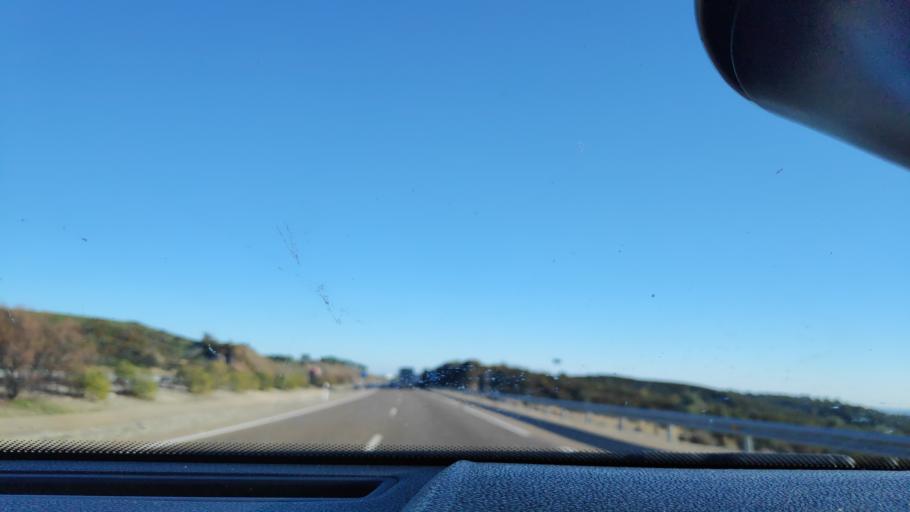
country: ES
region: Andalusia
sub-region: Provincia de Sevilla
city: Gerena
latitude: 37.5787
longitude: -6.1153
